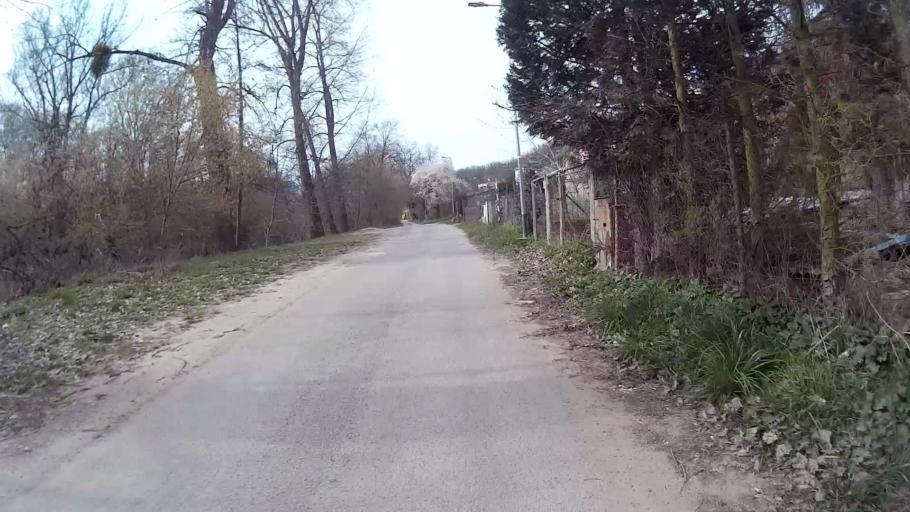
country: CZ
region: South Moravian
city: Dolni Kounice
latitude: 49.0640
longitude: 16.4786
